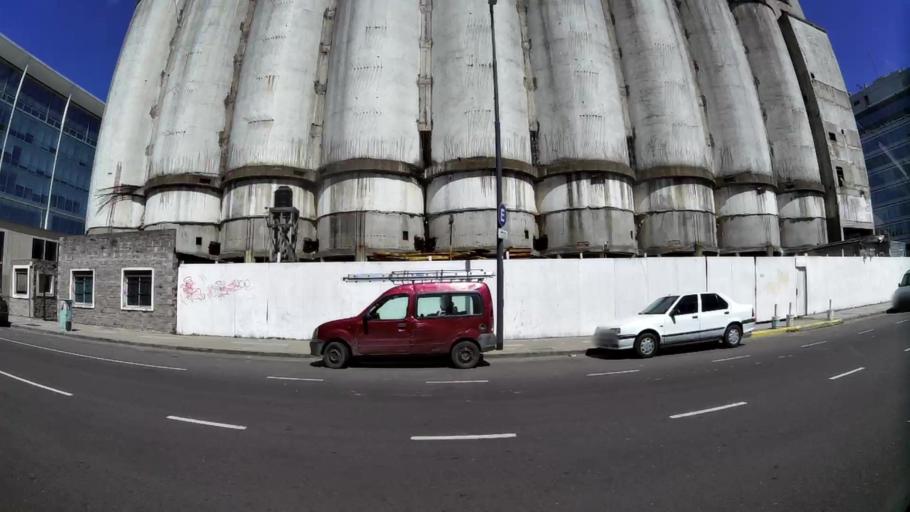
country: AR
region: Buenos Aires F.D.
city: Buenos Aires
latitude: -34.6077
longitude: -58.3630
